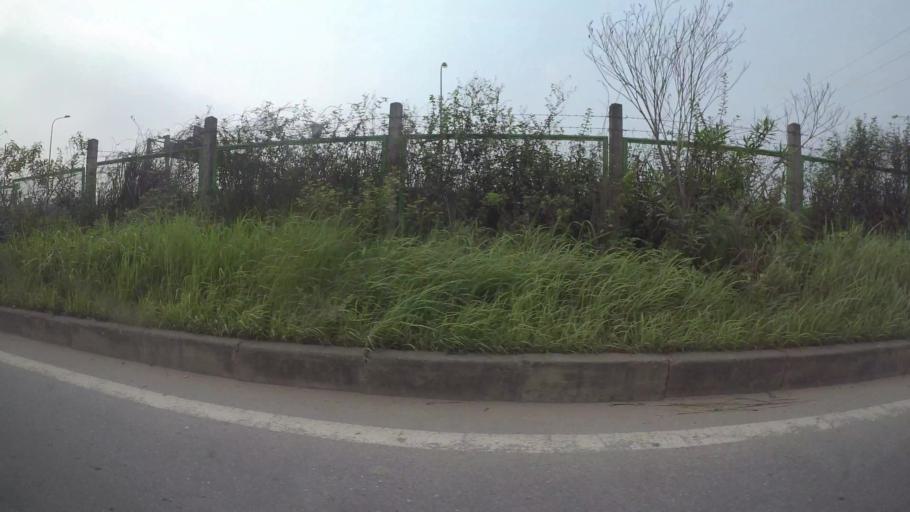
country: VN
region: Ha Noi
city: Quoc Oai
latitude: 21.0033
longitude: 105.6331
